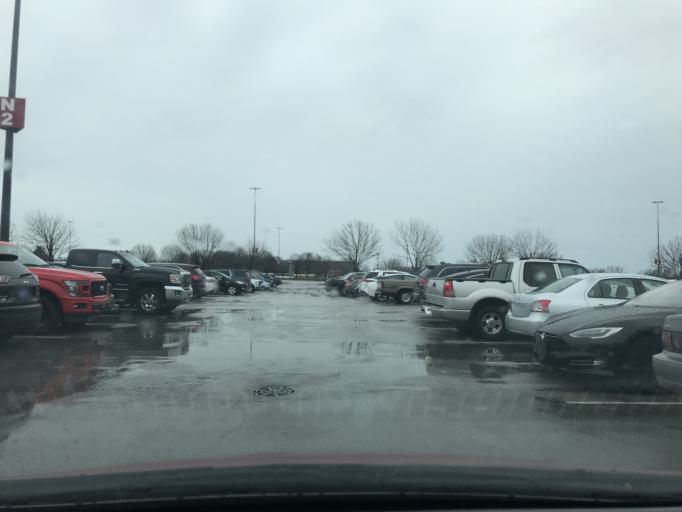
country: US
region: Kentucky
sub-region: Jefferson County
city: Audubon Park
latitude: 38.1980
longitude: -85.7426
